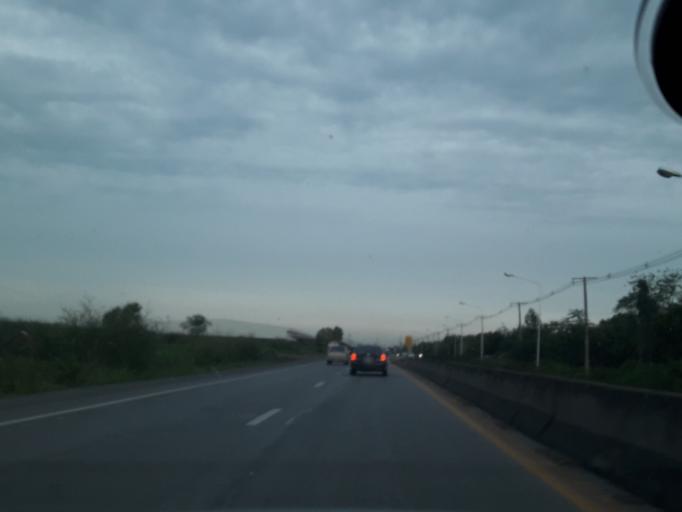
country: TH
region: Pathum Thani
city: Ban Rangsit
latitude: 14.0396
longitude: 100.7491
